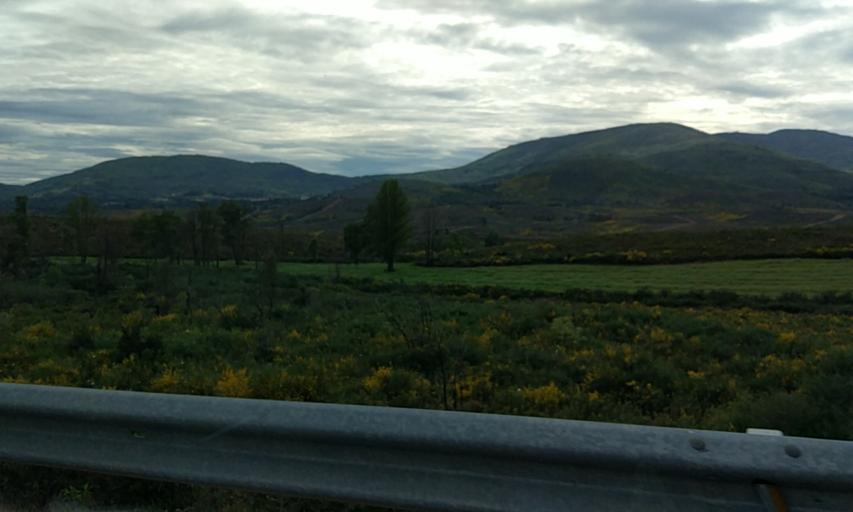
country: ES
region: Extremadura
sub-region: Provincia de Caceres
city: Perales del Puerto
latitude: 40.1952
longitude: -6.6761
